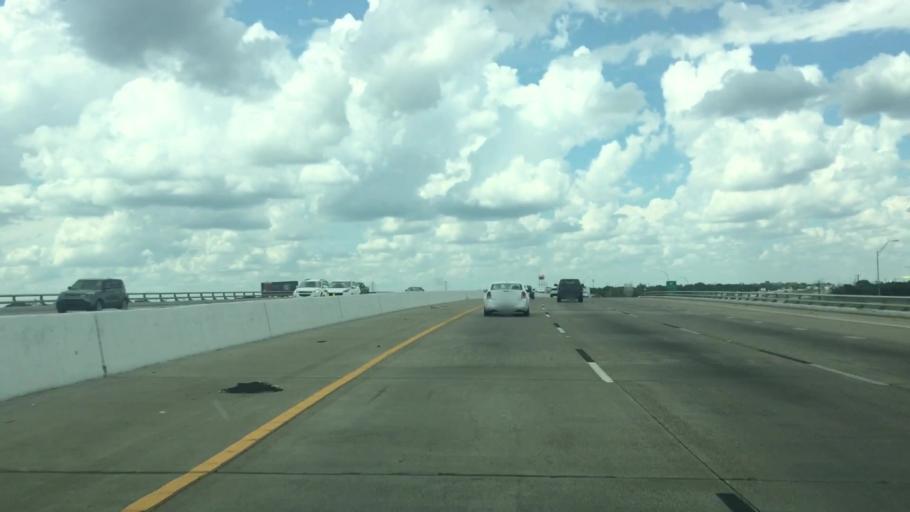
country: US
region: Texas
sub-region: McLennan County
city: Northcrest
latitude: 31.6504
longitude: -97.1000
